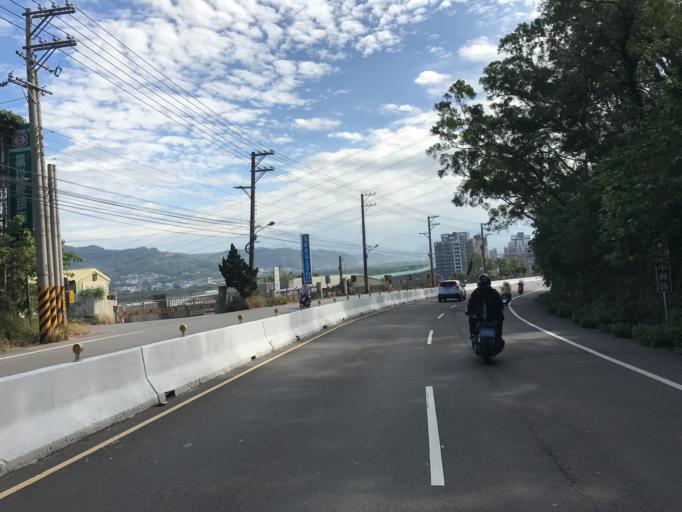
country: TW
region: Taiwan
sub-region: Hsinchu
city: Zhubei
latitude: 24.7522
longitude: 121.0766
